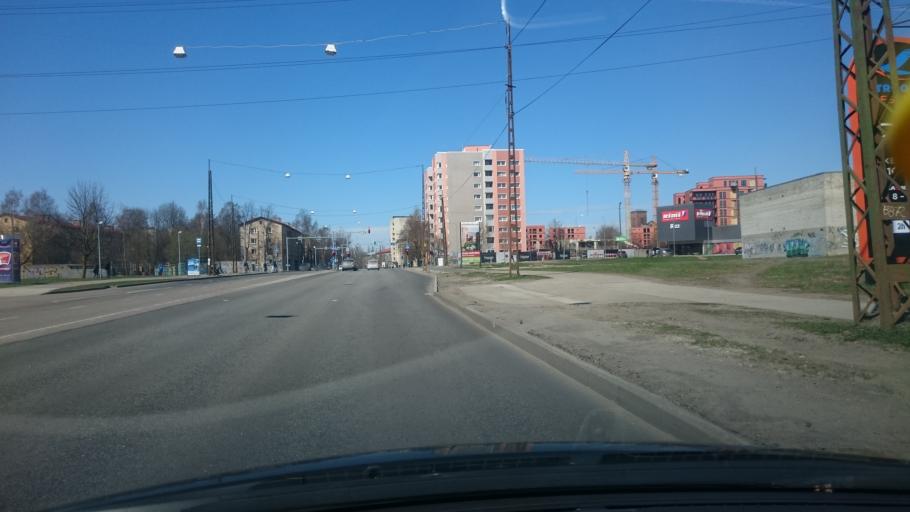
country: EE
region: Harju
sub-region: Tallinna linn
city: Tallinn
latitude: 59.4455
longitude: 24.7018
